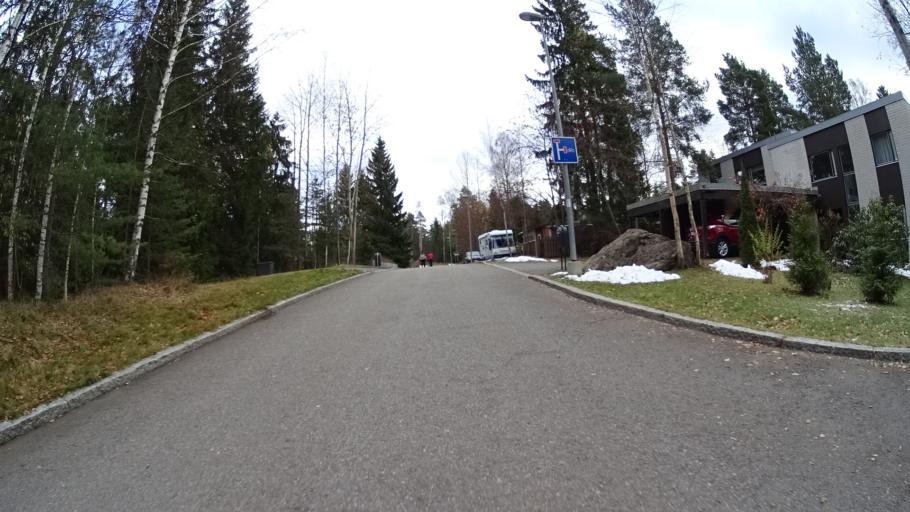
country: FI
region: Uusimaa
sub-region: Helsinki
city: Kilo
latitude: 60.2651
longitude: 24.8335
